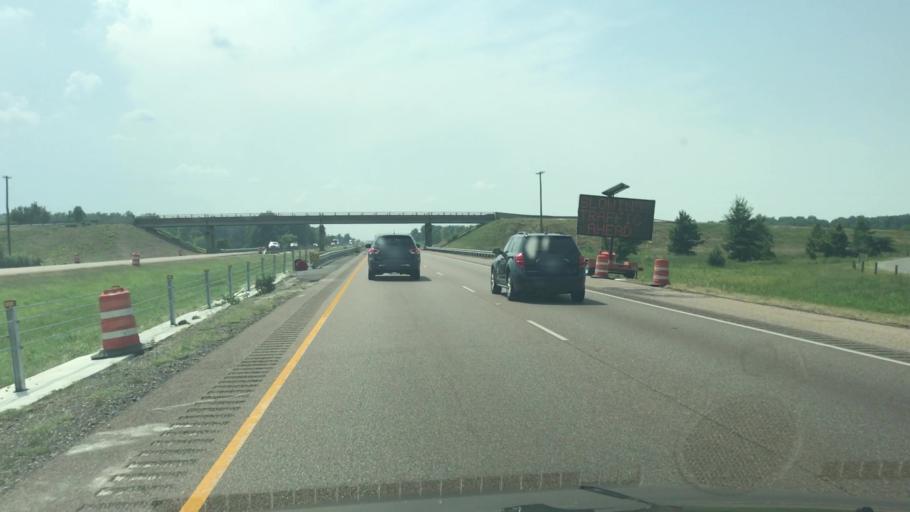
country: US
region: Arkansas
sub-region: Crittenden County
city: Earle
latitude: 35.1499
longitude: -90.3620
